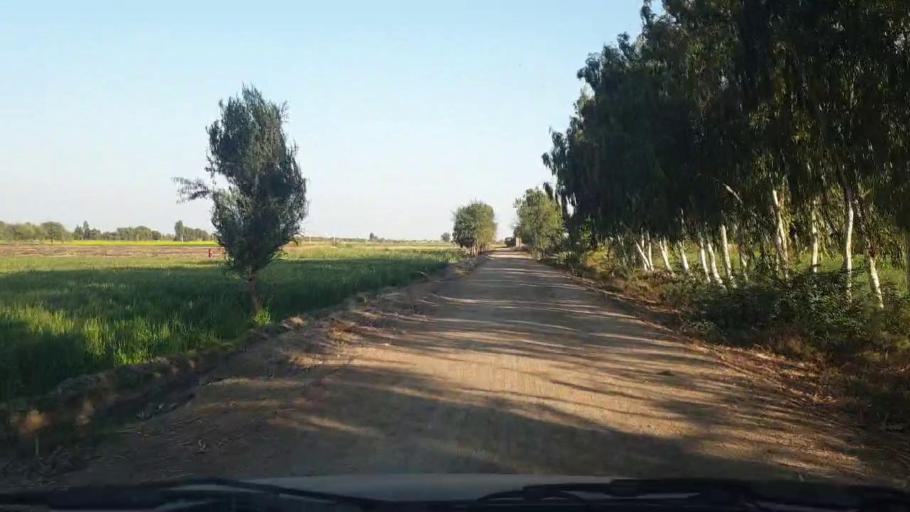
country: PK
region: Sindh
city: Samaro
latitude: 25.3395
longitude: 69.3140
